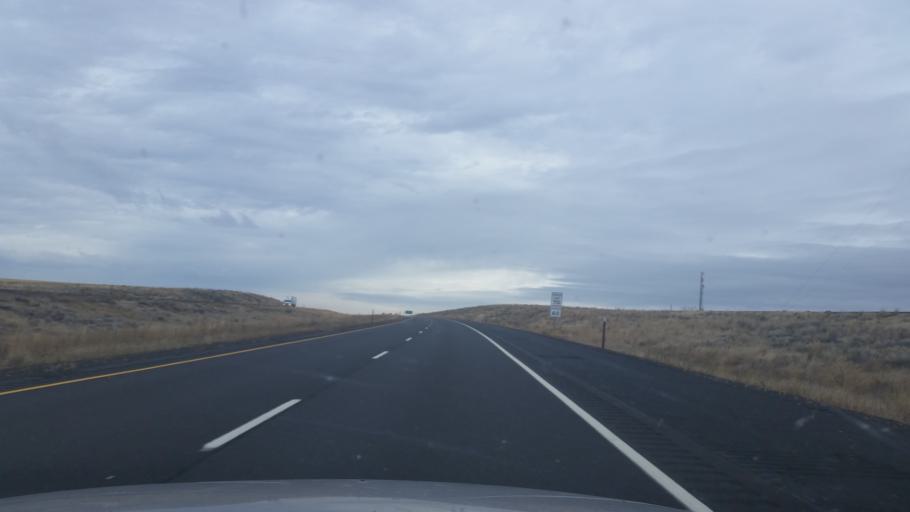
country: US
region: Washington
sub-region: Adams County
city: Ritzville
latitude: 47.0970
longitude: -118.6828
